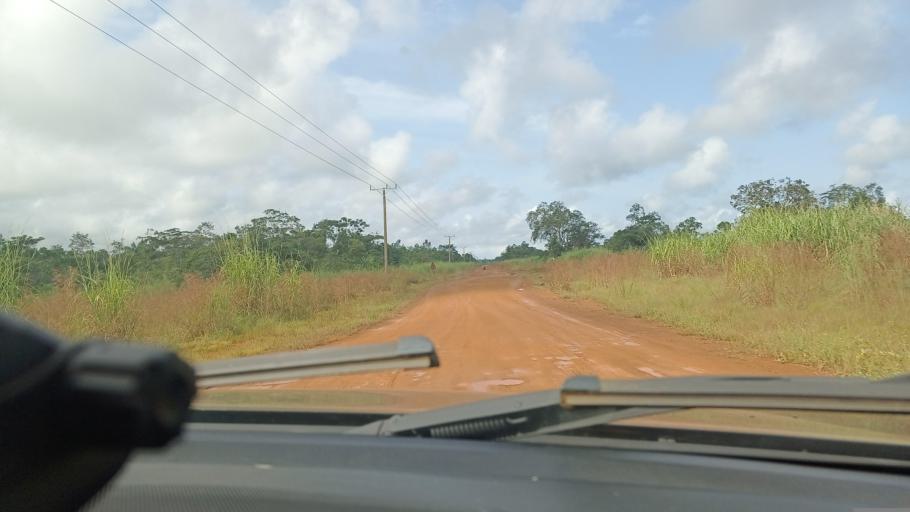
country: LR
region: Grand Cape Mount
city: Robertsport
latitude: 6.6858
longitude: -11.1227
